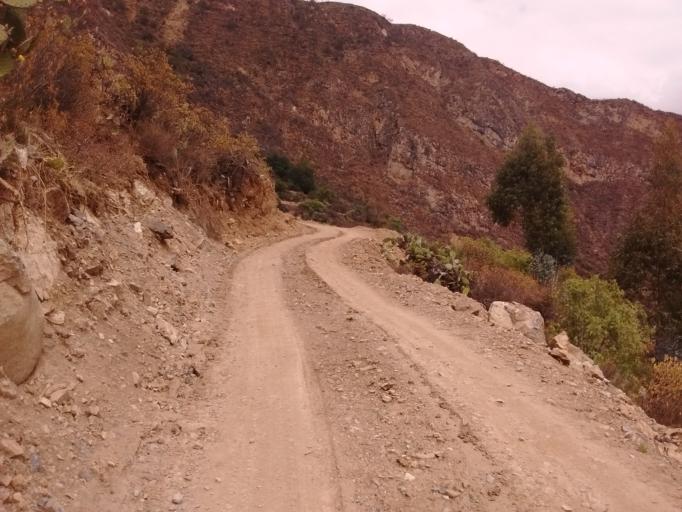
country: PE
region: Ayacucho
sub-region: Provincia de Victor Fajardo
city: Canaria
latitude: -13.8794
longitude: -73.9379
